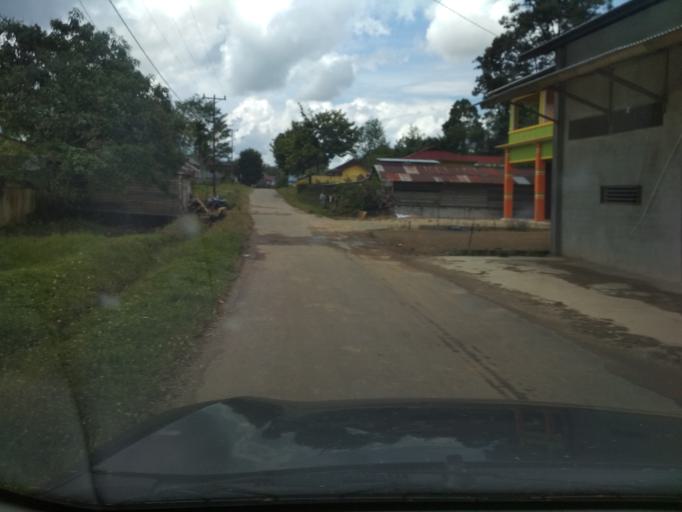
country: ID
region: West Kalimantan
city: Bengkayang
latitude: 0.7475
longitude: 110.1091
